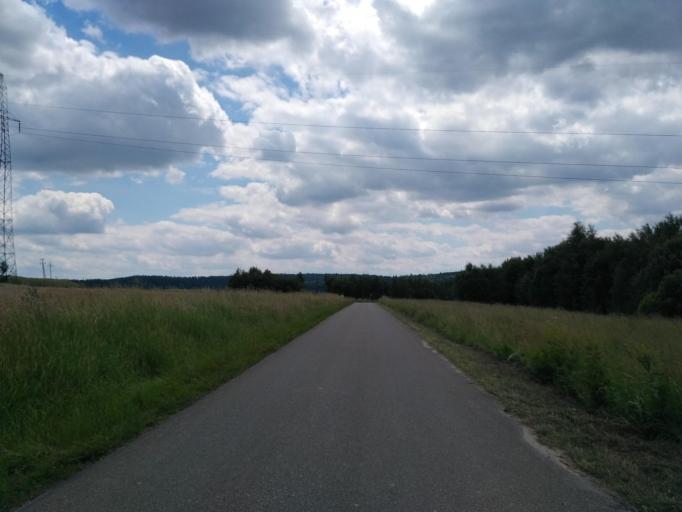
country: PL
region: Subcarpathian Voivodeship
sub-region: Powiat brzozowski
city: Nozdrzec
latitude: 49.7644
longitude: 22.1952
